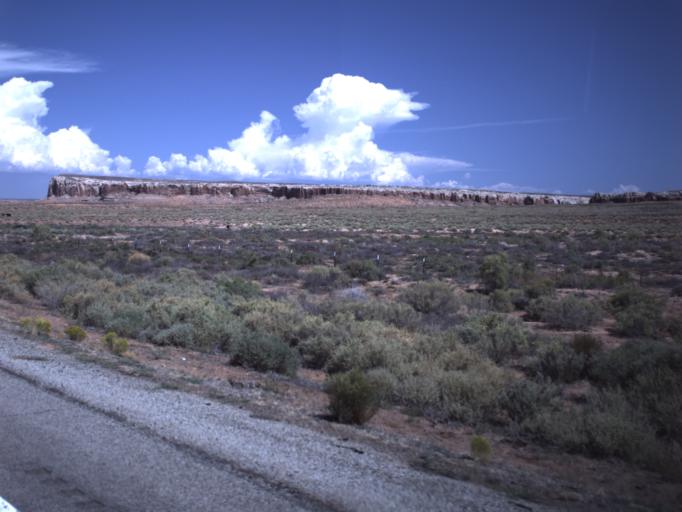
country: US
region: Utah
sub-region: San Juan County
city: Blanding
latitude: 37.2066
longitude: -109.6079
